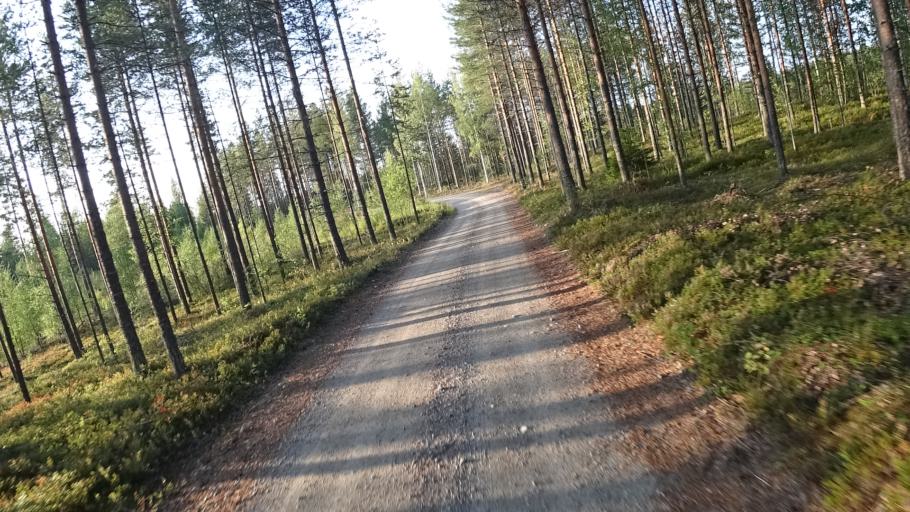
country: FI
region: North Karelia
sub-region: Joensuu
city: Ilomantsi
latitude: 62.6358
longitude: 31.0807
